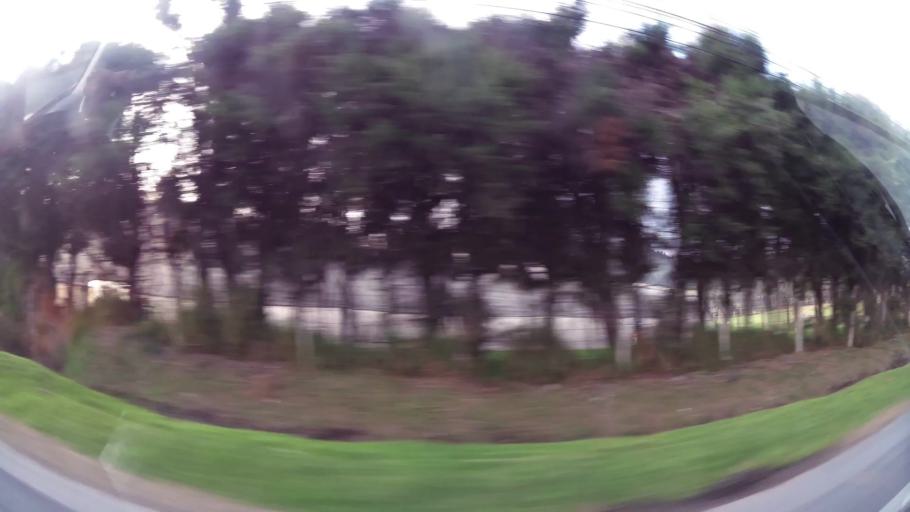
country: CO
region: Cundinamarca
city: Cota
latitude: 4.7815
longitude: -74.1342
